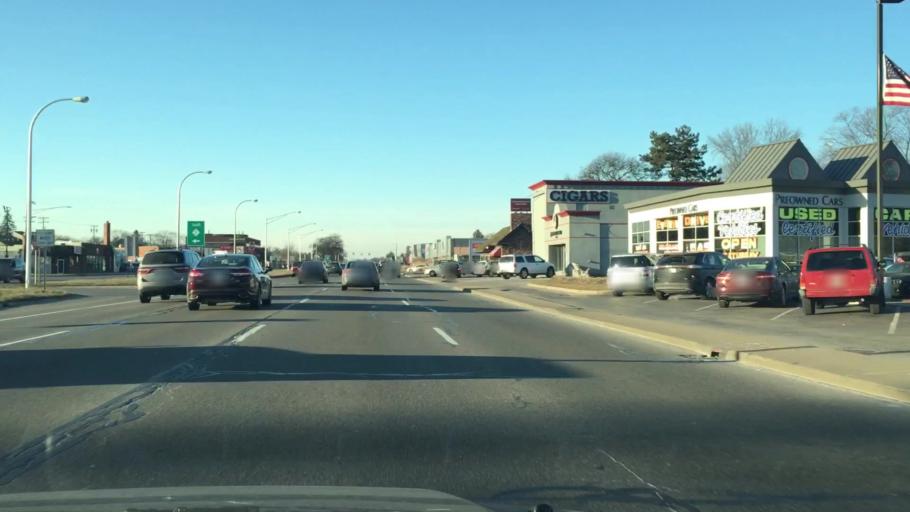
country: US
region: Michigan
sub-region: Oakland County
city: Huntington Woods
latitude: 42.4936
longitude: -83.1625
